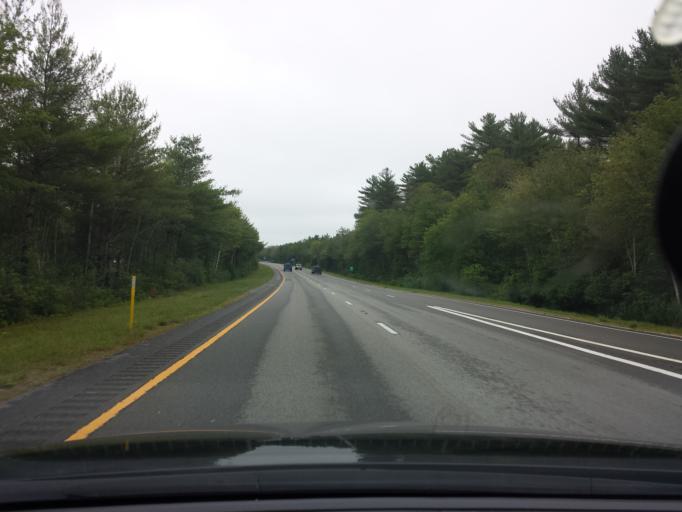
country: US
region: Massachusetts
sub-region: Plymouth County
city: Marion Center
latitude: 41.7264
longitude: -70.7734
